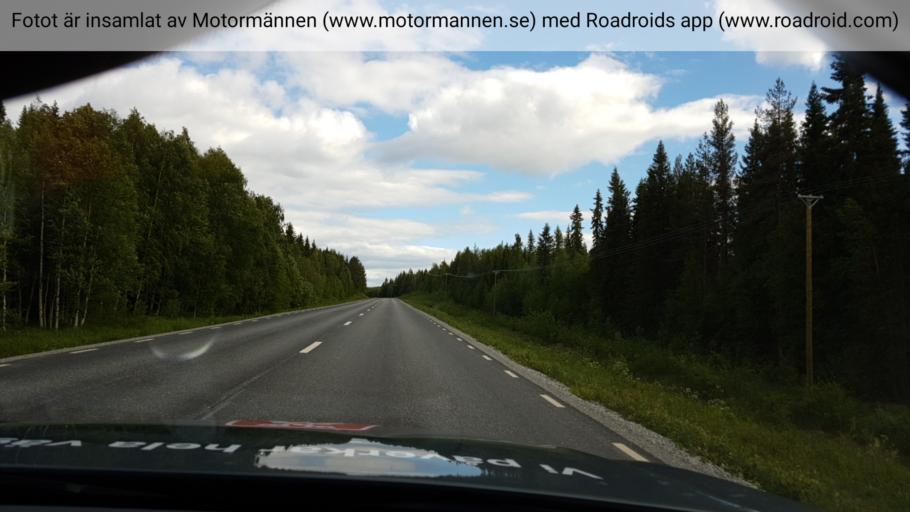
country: SE
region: Jaemtland
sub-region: Stroemsunds Kommun
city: Stroemsund
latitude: 64.2041
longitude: 15.5941
